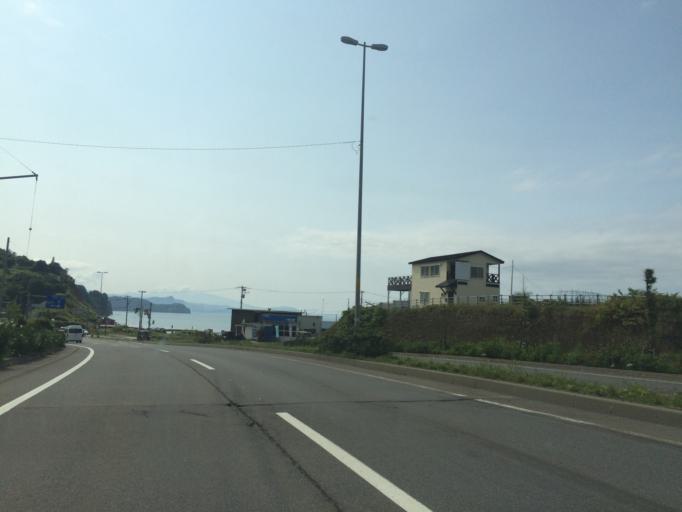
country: JP
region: Hokkaido
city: Otaru
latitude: 43.2107
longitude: 140.9178
